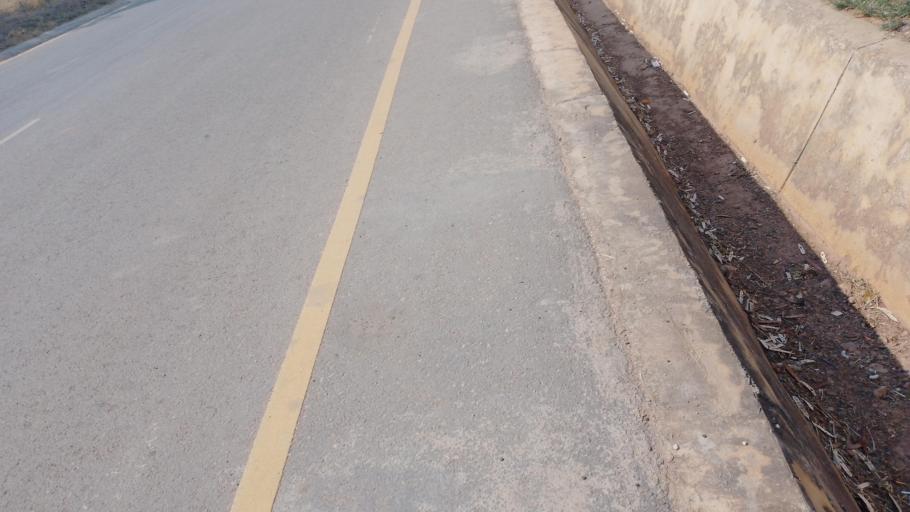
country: ZM
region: Lusaka
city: Lusaka
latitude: -15.3927
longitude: 28.3929
